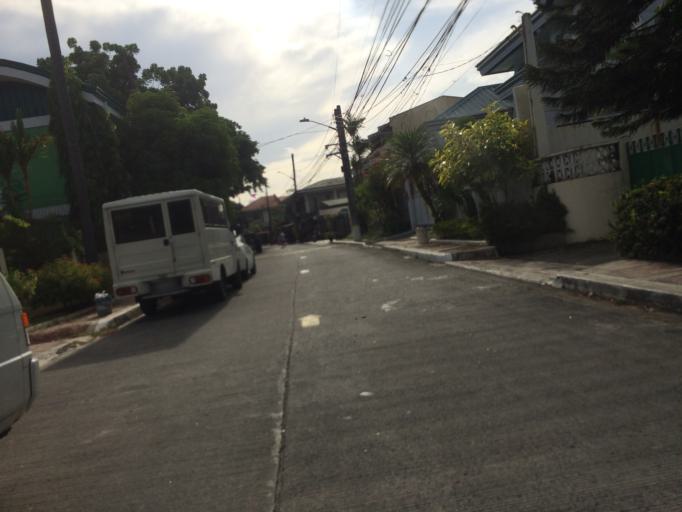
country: PH
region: Calabarzon
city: Bagong Pagasa
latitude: 14.6705
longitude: 121.0214
